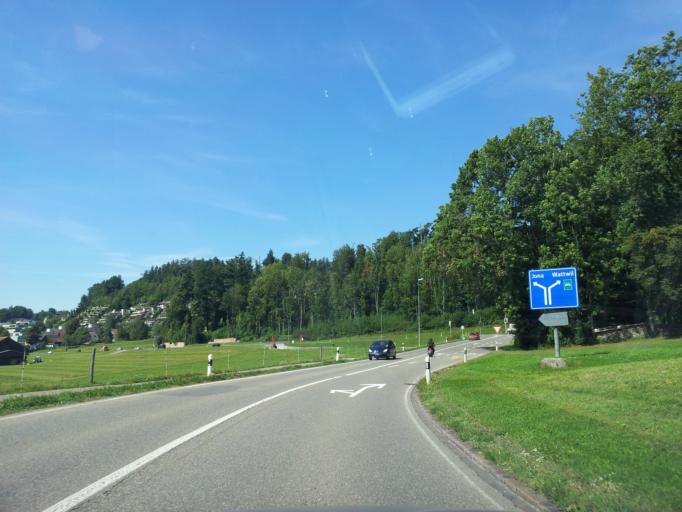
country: CH
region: Saint Gallen
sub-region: Wahlkreis See-Gaster
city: Jona
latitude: 47.2281
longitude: 8.8595
